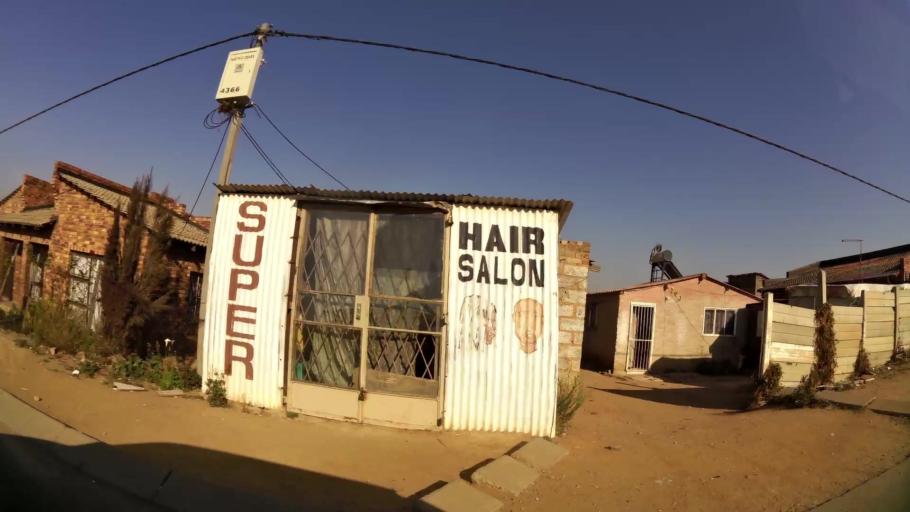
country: ZA
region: Gauteng
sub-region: City of Johannesburg Metropolitan Municipality
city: Modderfontein
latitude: -26.0991
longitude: 28.1149
